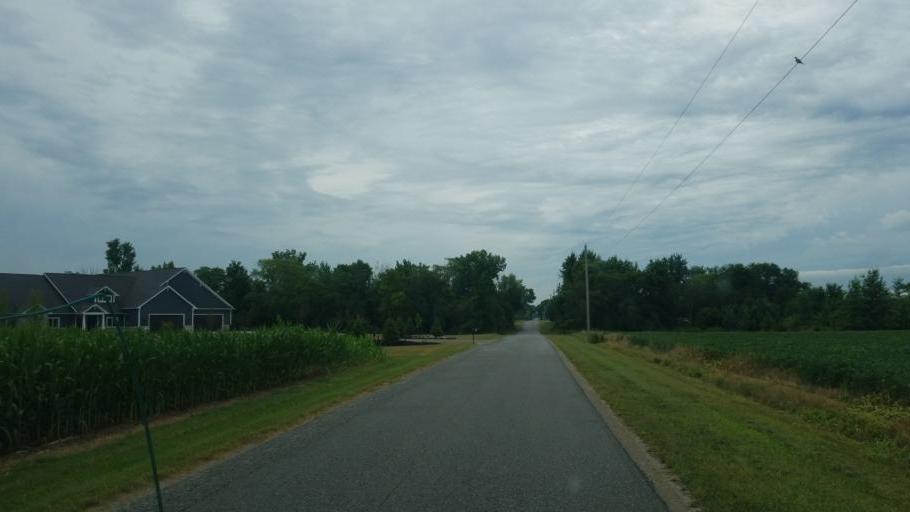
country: US
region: Ohio
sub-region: Paulding County
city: Antwerp
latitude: 41.2438
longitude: -84.6893
